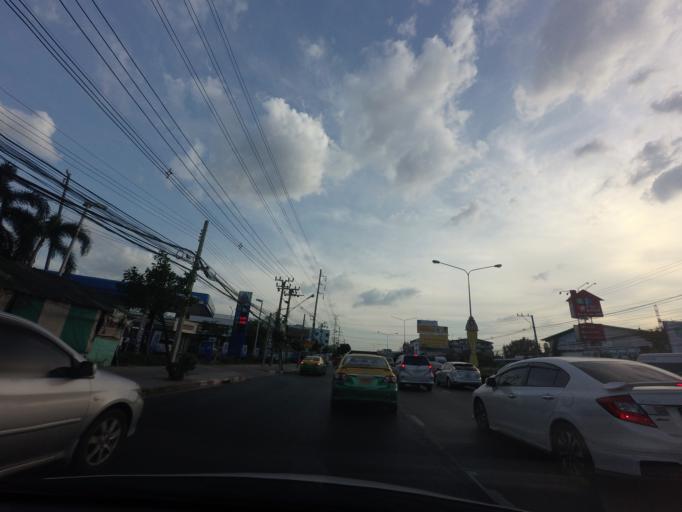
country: TH
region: Bangkok
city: Bang Khun Thian
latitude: 13.6508
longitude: 100.4310
